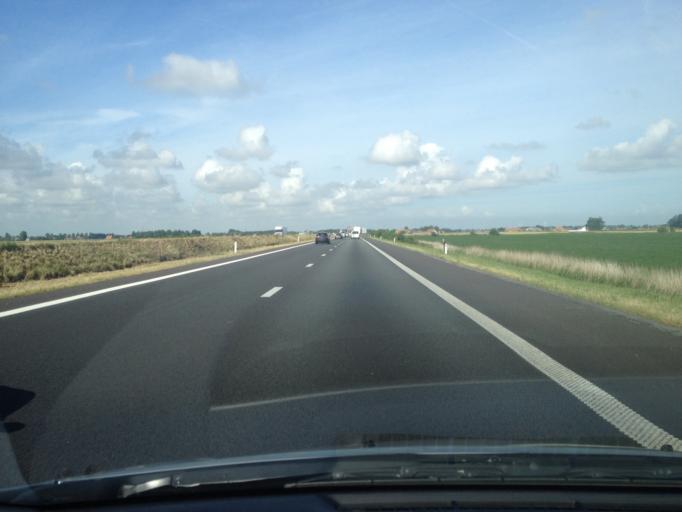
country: BE
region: Flanders
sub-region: Provincie West-Vlaanderen
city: Middelkerke
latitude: 51.1382
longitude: 2.8388
